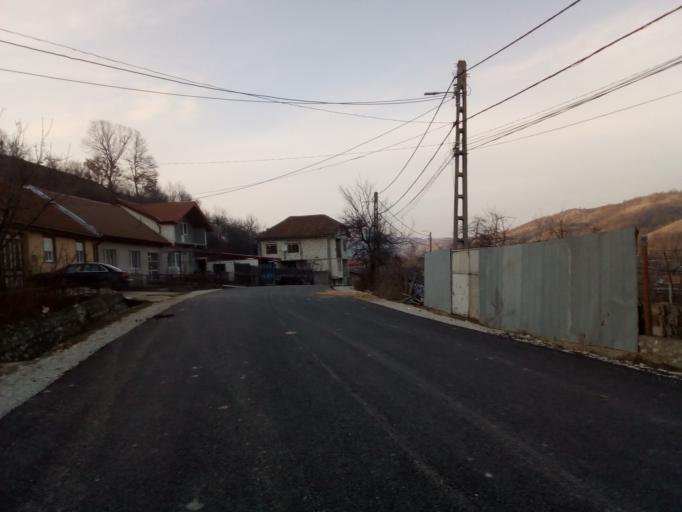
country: RO
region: Mehedinti
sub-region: Comuna Eselnita
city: Eselnita
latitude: 44.6928
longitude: 22.3633
